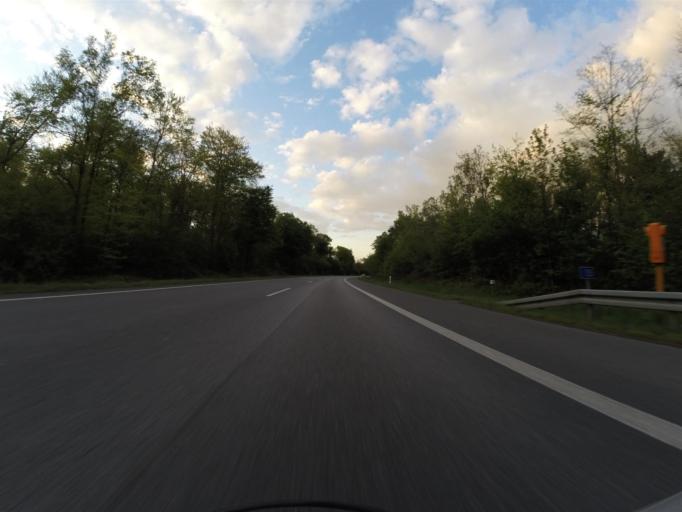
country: DE
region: Hesse
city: Raunheim
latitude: 50.0249
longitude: 8.4969
